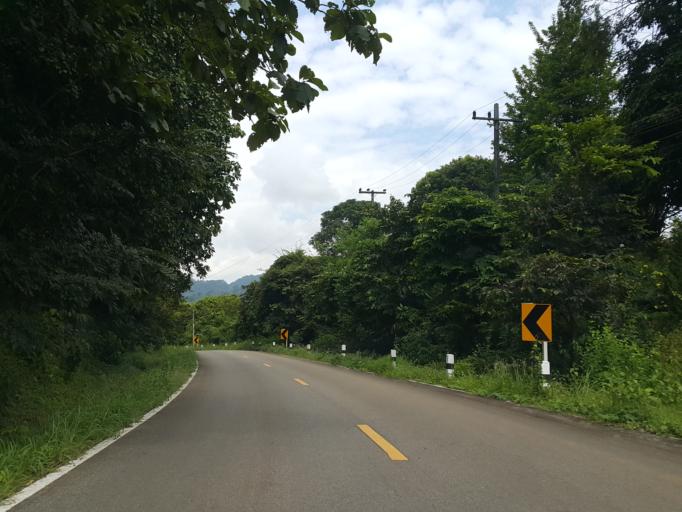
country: TH
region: Mae Hong Son
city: Mae Hong Son
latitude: 19.4760
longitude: 97.9663
